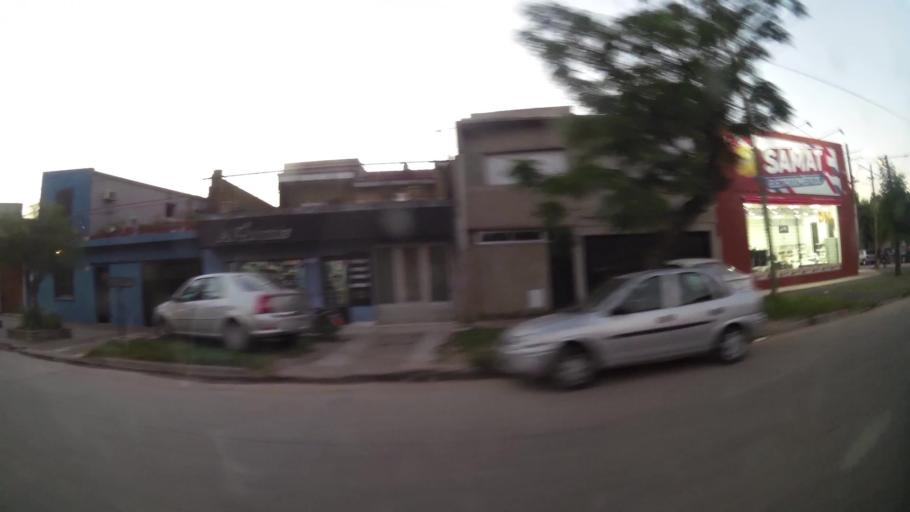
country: AR
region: Santa Fe
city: Santa Fe de la Vera Cruz
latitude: -31.6094
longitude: -60.7132
